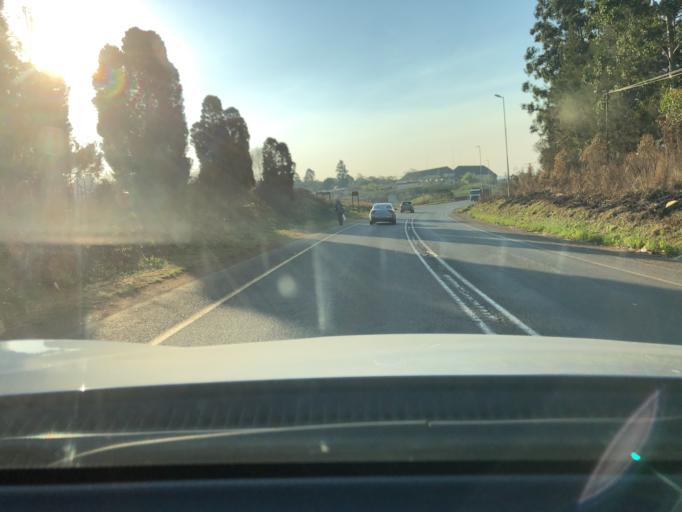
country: ZA
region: KwaZulu-Natal
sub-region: Sisonke District Municipality
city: Ixopo
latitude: -30.1529
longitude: 30.0756
